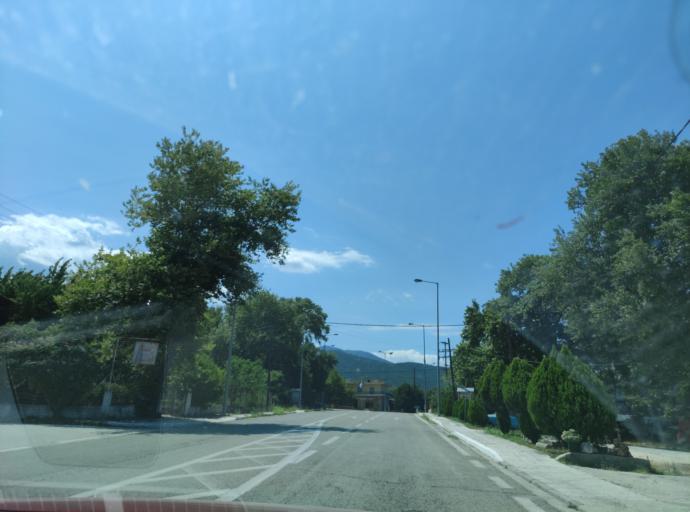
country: GR
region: East Macedonia and Thrace
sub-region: Nomos Kavalas
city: Palaiochori
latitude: 40.9529
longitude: 24.1952
